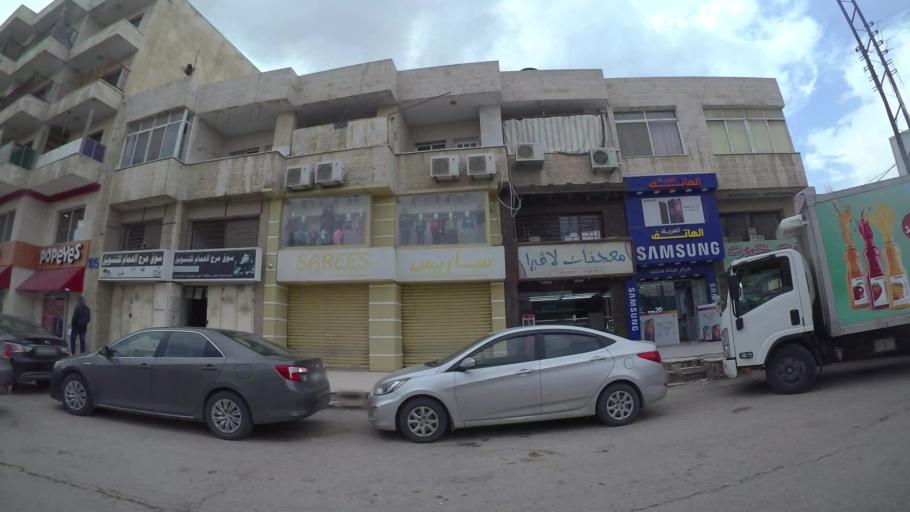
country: JO
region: Amman
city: Umm as Summaq
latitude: 31.8940
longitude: 35.8400
